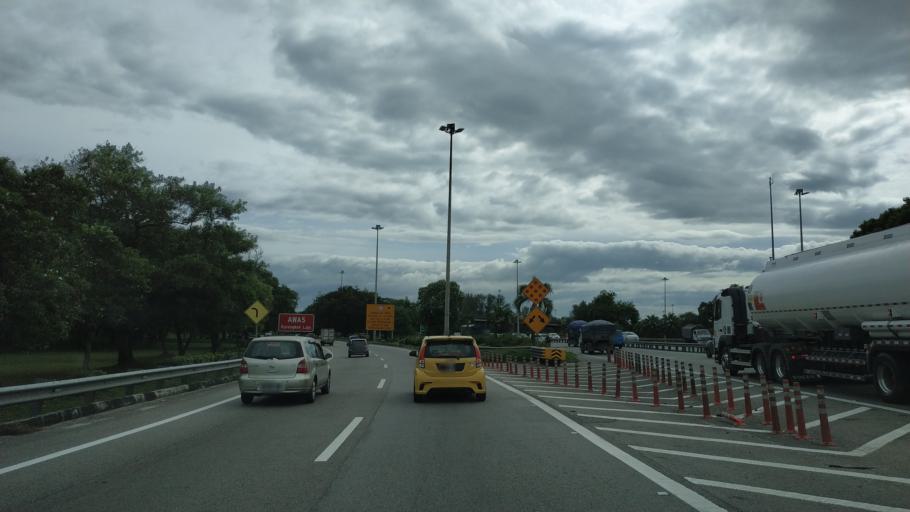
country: MY
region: Penang
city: Perai
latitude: 5.3692
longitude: 100.3996
